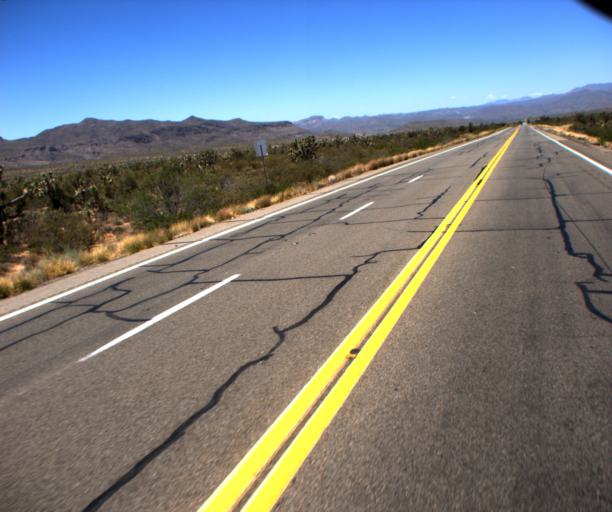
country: US
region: Arizona
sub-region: Yavapai County
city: Congress
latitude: 34.2892
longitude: -113.1094
